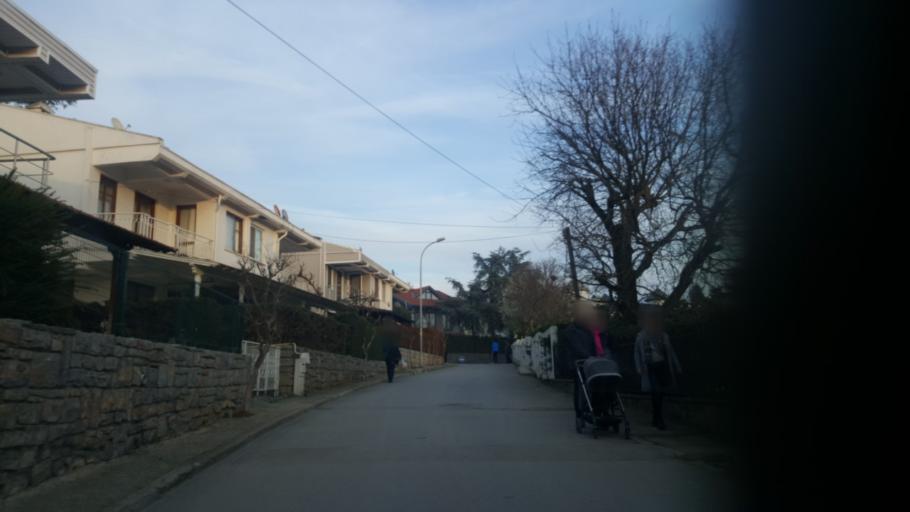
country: TR
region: Istanbul
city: Icmeler
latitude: 40.8185
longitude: 29.2708
